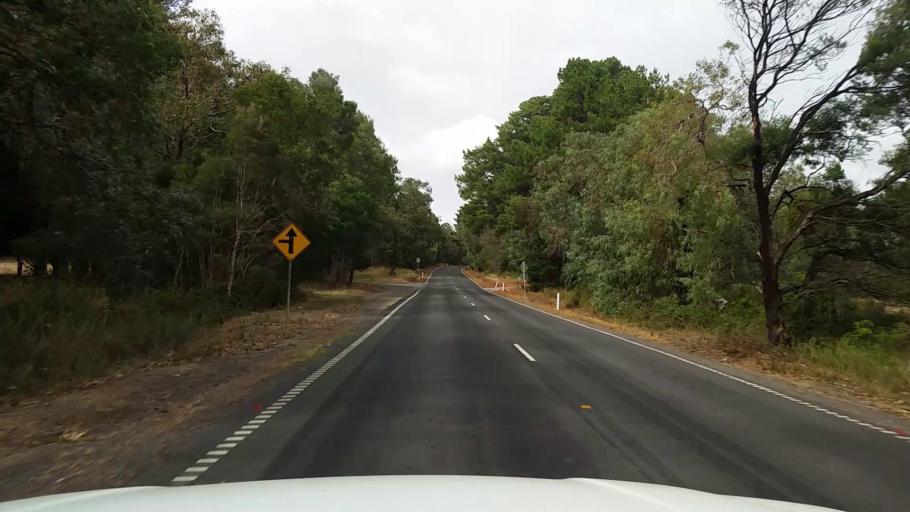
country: AU
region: Victoria
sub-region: Mornington Peninsula
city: Balnarring
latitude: -38.3234
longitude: 145.0916
